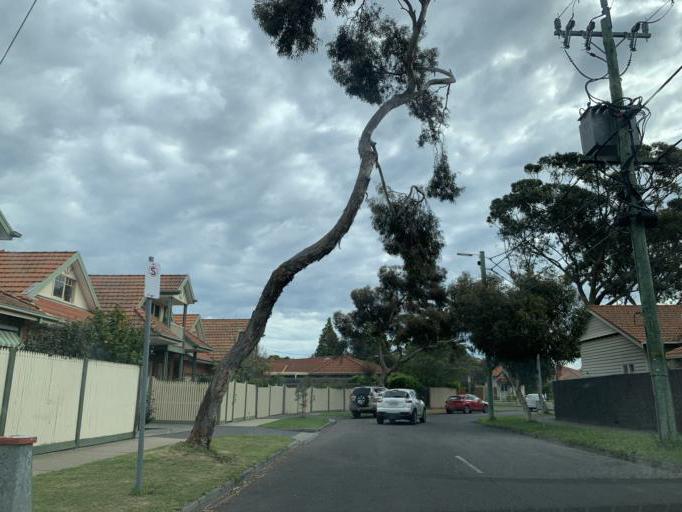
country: AU
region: Victoria
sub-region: Bayside
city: Hampton
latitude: -37.9318
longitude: 145.0101
